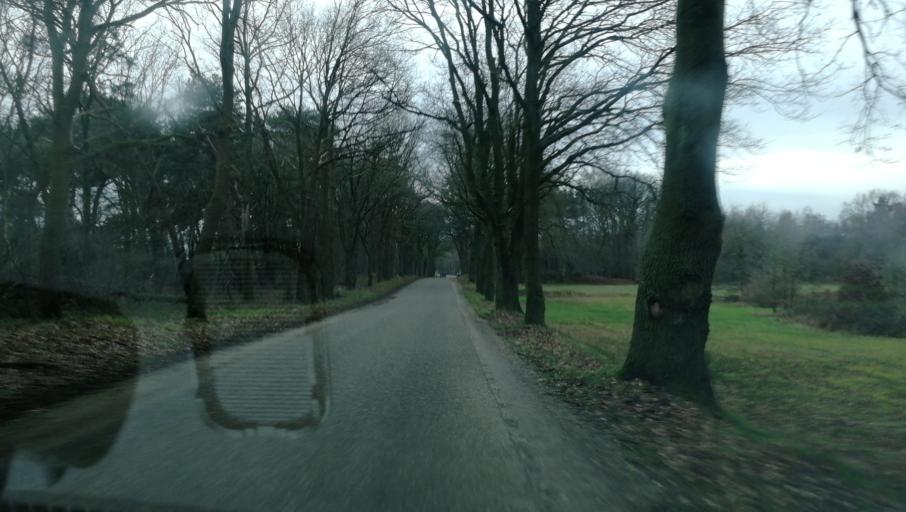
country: NL
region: Limburg
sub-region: Gemeente Venlo
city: Venlo
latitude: 51.4105
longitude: 6.1921
